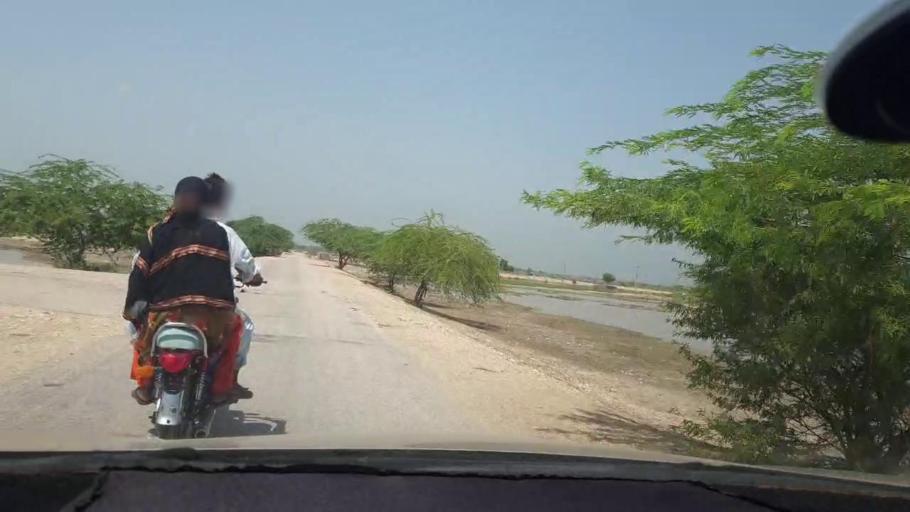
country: PK
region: Sindh
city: Kambar
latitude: 27.6747
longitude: 67.9113
